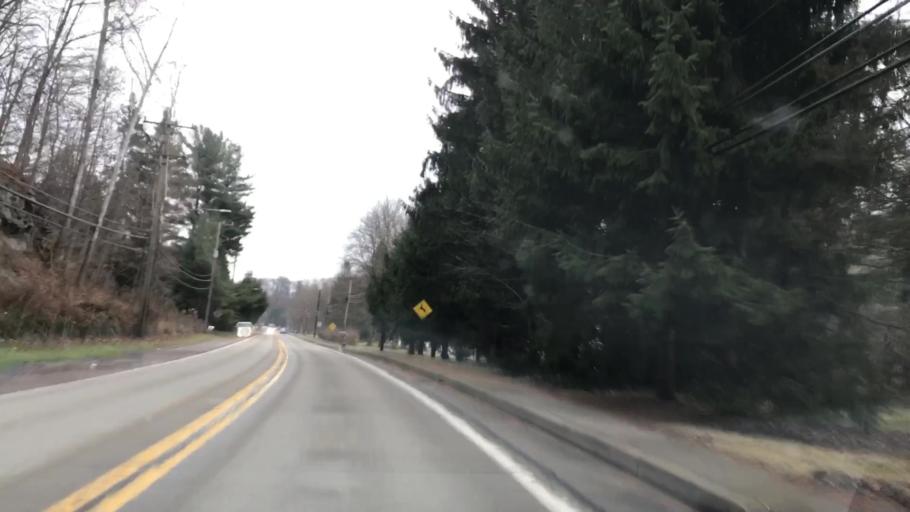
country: US
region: Pennsylvania
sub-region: Allegheny County
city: Leetsdale
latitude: 40.5473
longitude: -80.2187
